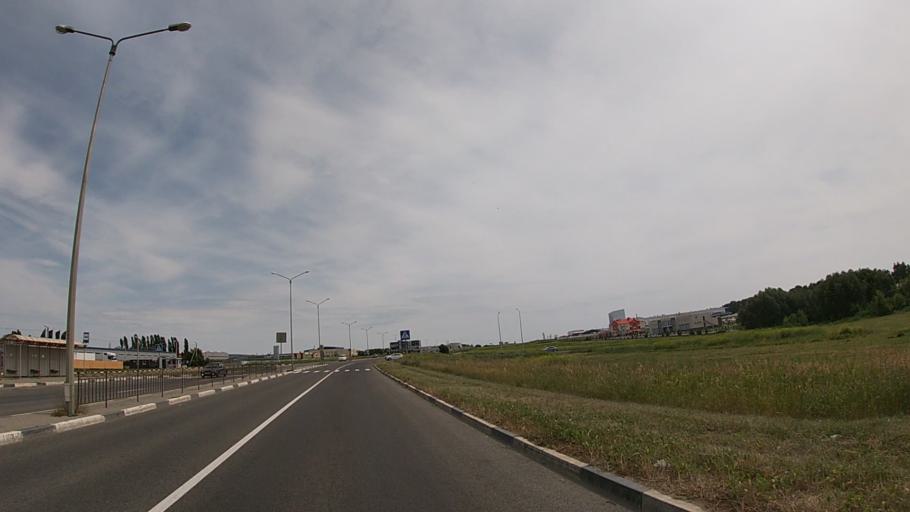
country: RU
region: Belgorod
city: Severnyy
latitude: 50.6584
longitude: 36.5493
